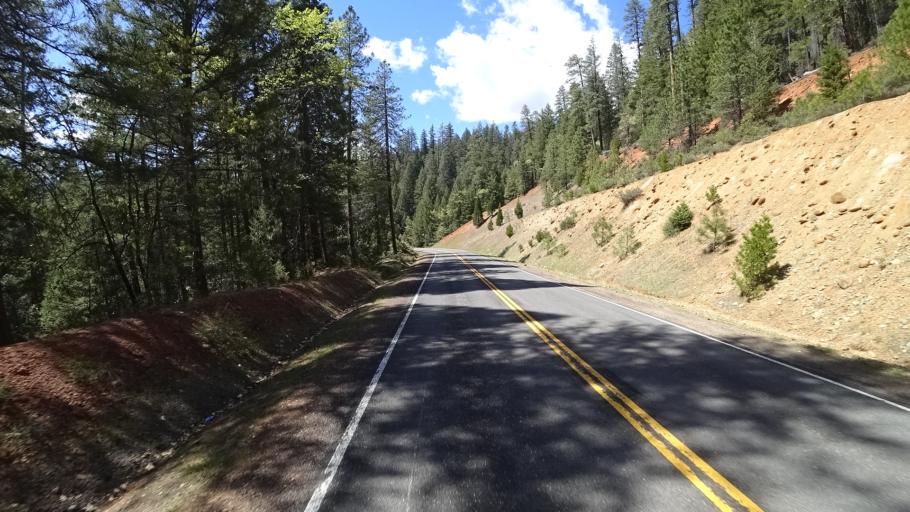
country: US
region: California
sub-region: Trinity County
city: Lewiston
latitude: 40.8462
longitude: -122.8407
